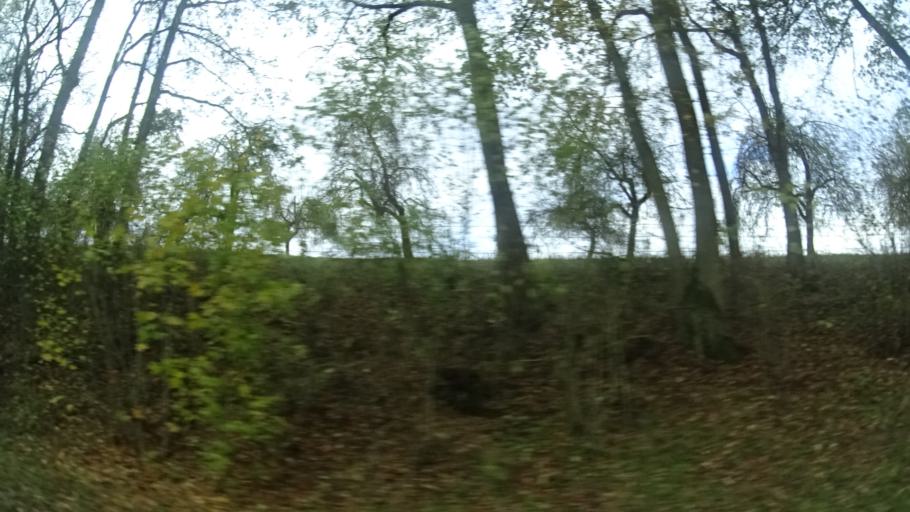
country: DE
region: Bavaria
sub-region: Regierungsbezirk Unterfranken
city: Hochheim
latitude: 50.3628
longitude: 10.4412
